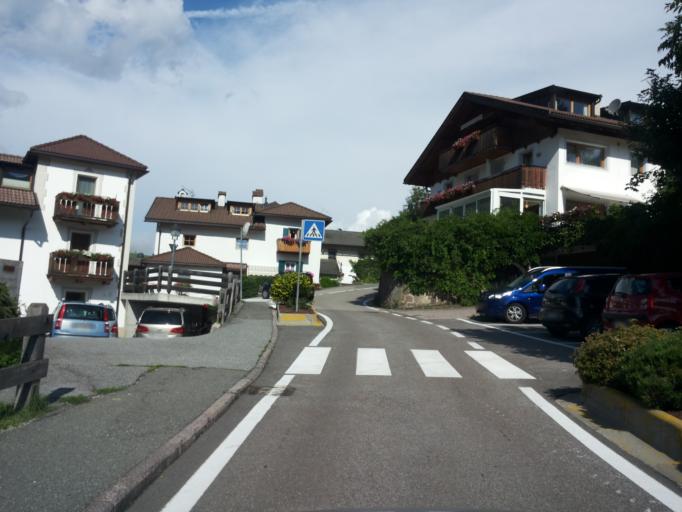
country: IT
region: Trentino-Alto Adige
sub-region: Bolzano
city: Ortisei
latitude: 46.5759
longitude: 11.6644
